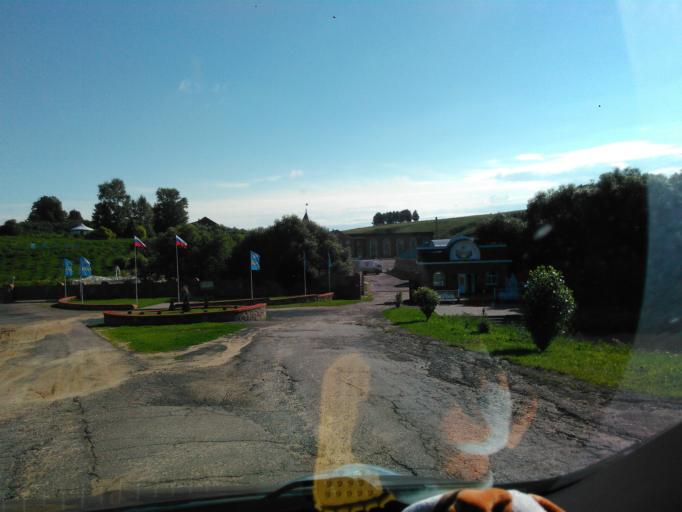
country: RU
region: Penza
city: Lermontovo
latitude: 53.1722
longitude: 44.1441
